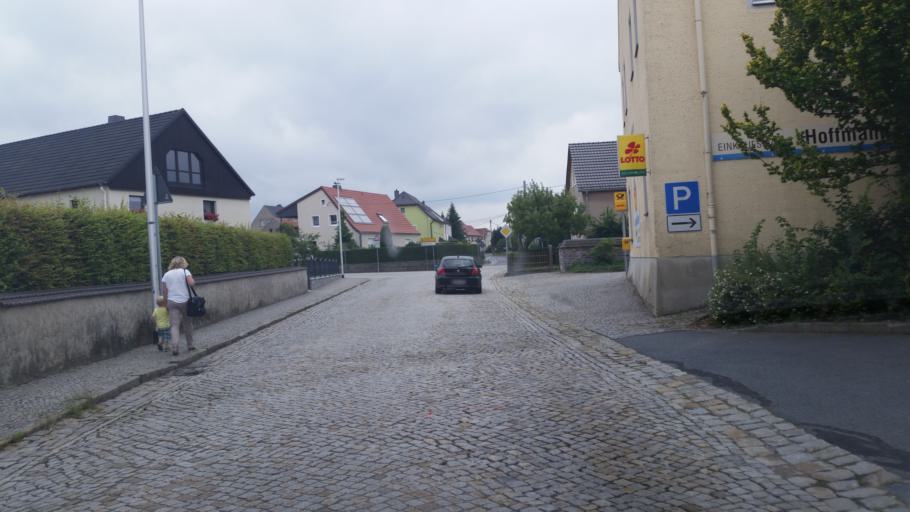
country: DE
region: Saxony
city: Laussnitz
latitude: 51.2466
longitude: 13.8807
